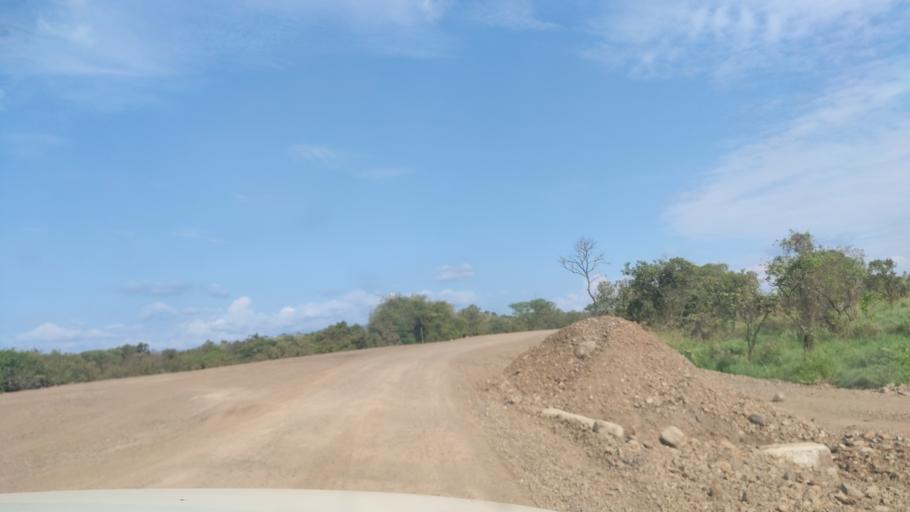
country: ET
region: Southern Nations, Nationalities, and People's Region
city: Felege Neway
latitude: 6.4292
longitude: 37.2113
